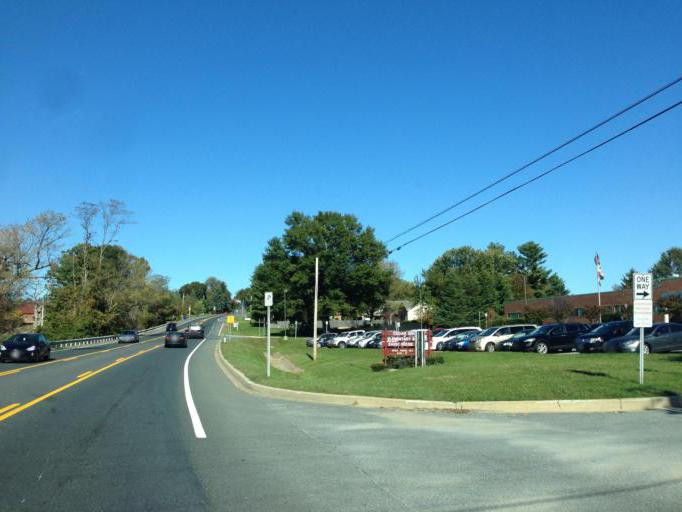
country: US
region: Maryland
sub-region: Montgomery County
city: Clarksburg
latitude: 39.2494
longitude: -77.2335
